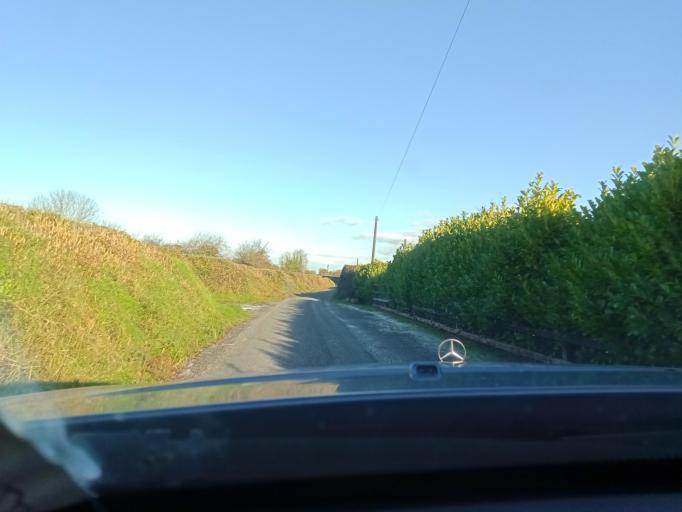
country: IE
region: Leinster
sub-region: Kilkenny
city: Graiguenamanagh
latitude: 52.5527
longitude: -6.9489
